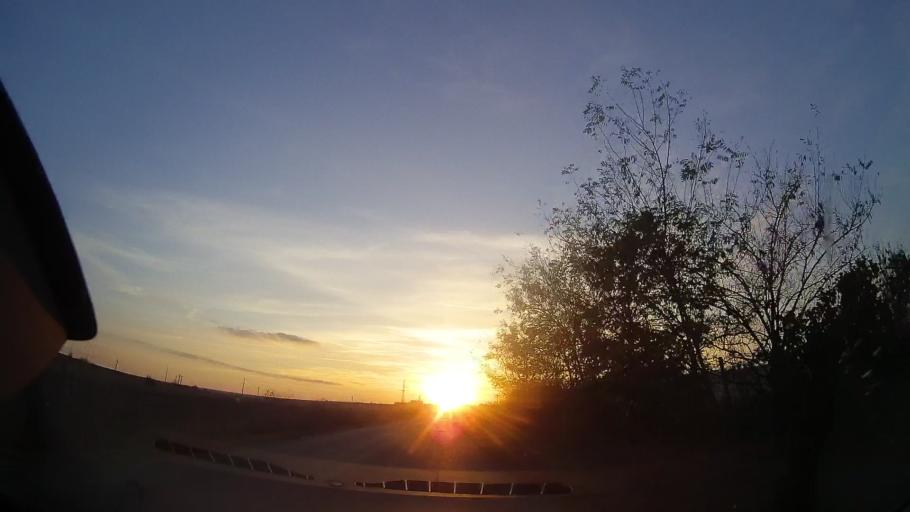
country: RO
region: Constanta
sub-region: Comuna Mereni
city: Mereni
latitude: 44.0279
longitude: 28.3701
